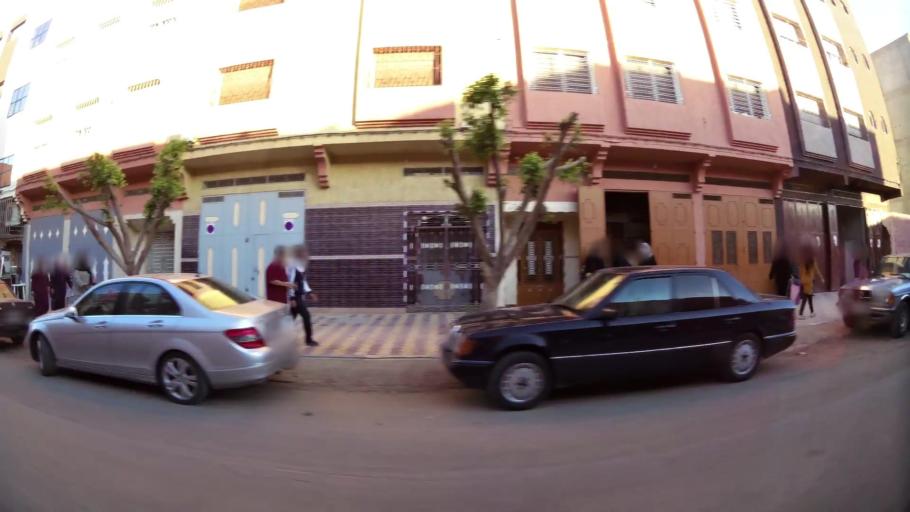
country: MA
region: Oriental
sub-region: Berkane-Taourirt
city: Berkane
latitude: 34.9219
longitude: -2.3196
